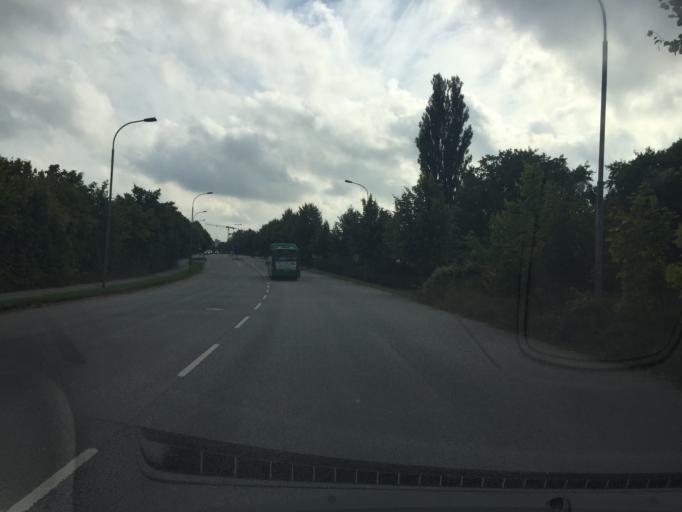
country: SE
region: Skane
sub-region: Lunds Kommun
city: Lund
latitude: 55.7183
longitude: 13.1855
